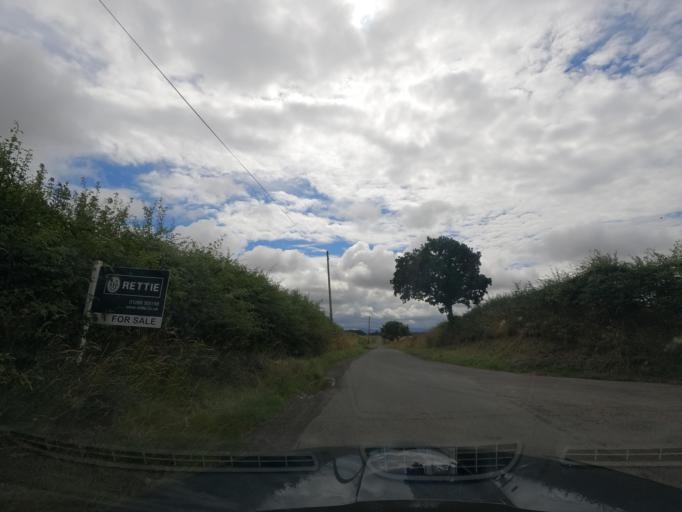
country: GB
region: Scotland
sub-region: The Scottish Borders
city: Allanton
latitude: 55.7265
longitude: -2.1963
